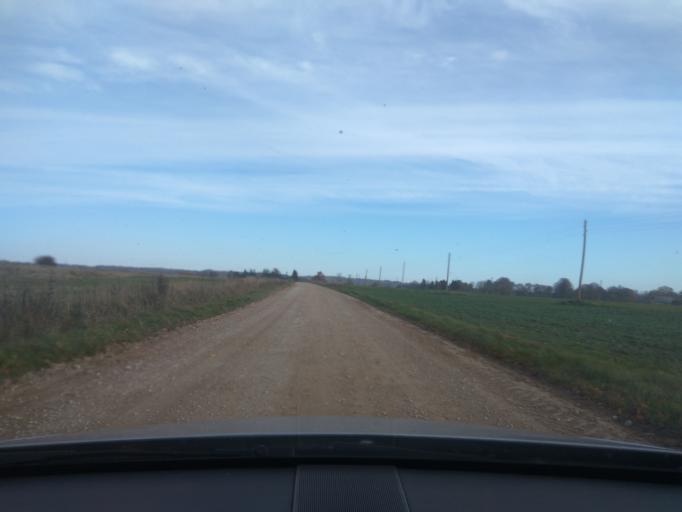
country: LV
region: Aizpute
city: Aizpute
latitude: 56.8588
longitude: 21.6675
